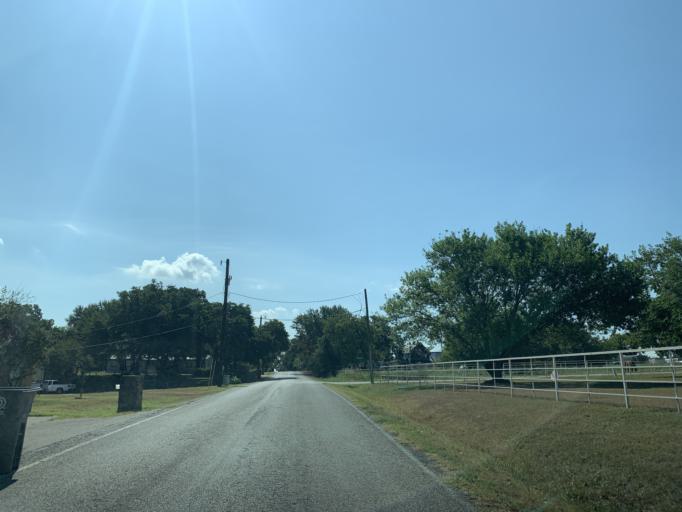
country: US
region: Texas
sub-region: Tarrant County
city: Azle
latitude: 32.8633
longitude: -97.5261
